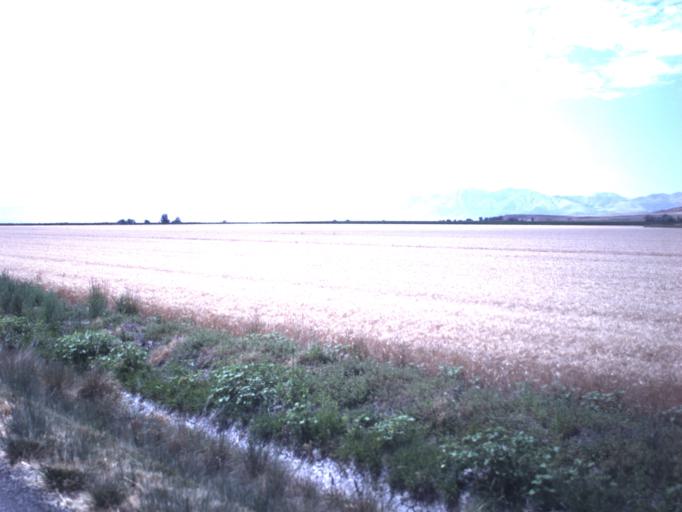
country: US
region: Utah
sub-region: Box Elder County
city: Tremonton
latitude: 41.6421
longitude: -112.3141
